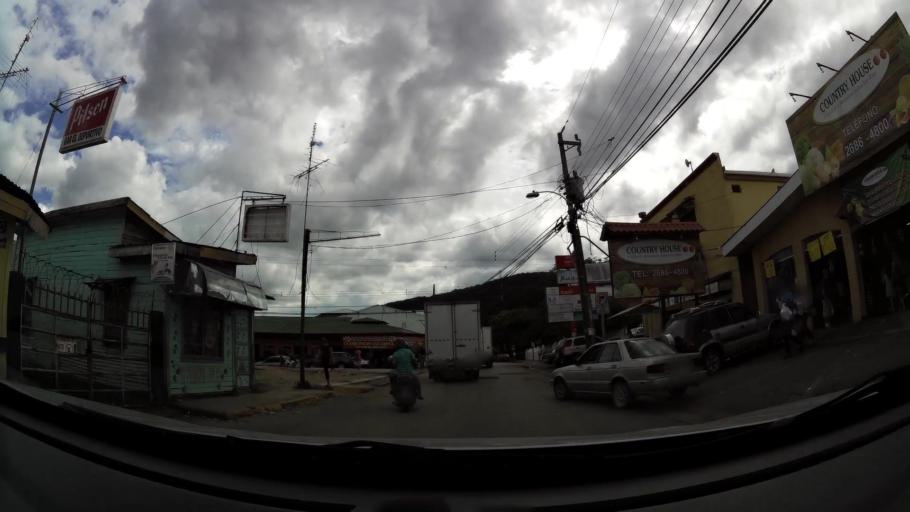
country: CR
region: Guanacaste
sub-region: Canton de Nicoya
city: Nicoya
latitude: 10.1436
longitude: -85.4531
